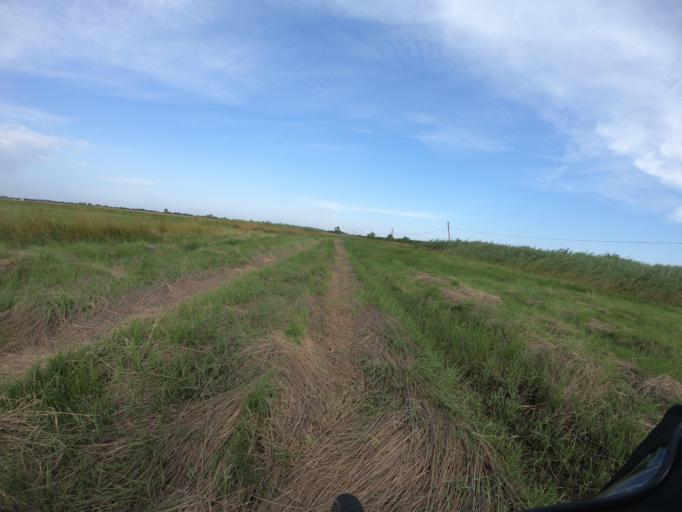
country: HU
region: Hajdu-Bihar
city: Tiszacsege
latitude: 47.6117
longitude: 21.0335
